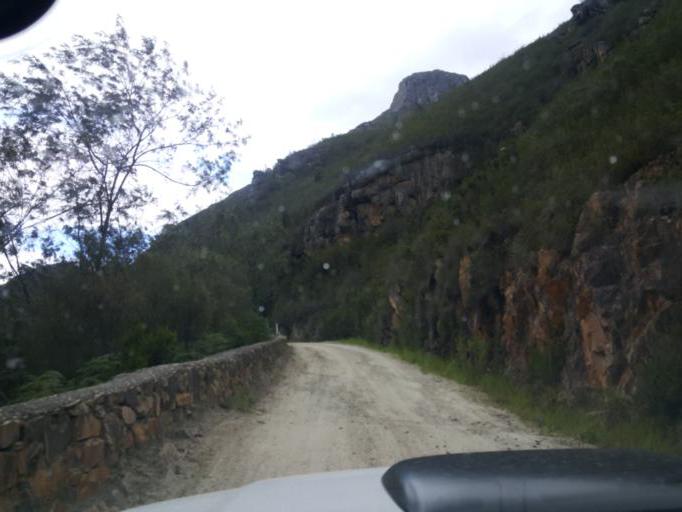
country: ZA
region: Western Cape
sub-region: Eden District Municipality
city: George
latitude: -33.8983
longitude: 22.4161
